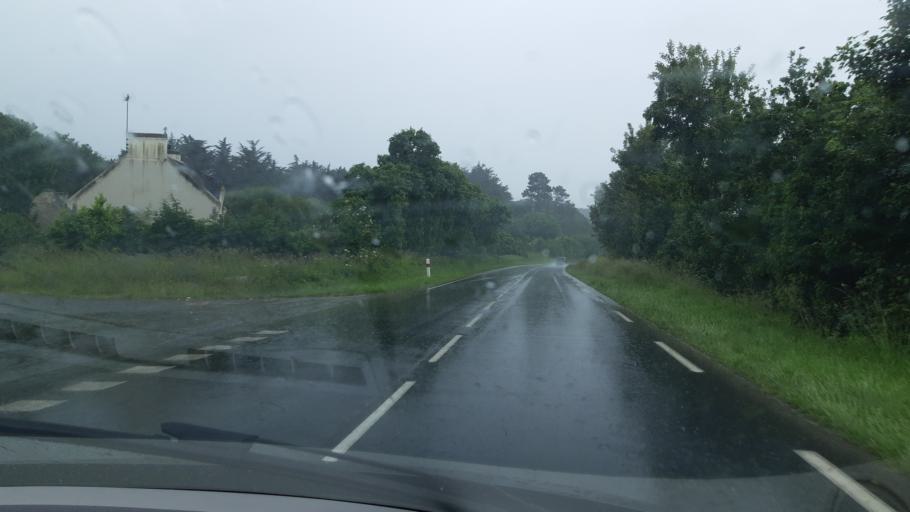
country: FR
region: Brittany
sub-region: Departement du Finistere
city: Plougoulm
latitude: 48.6599
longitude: -4.0237
